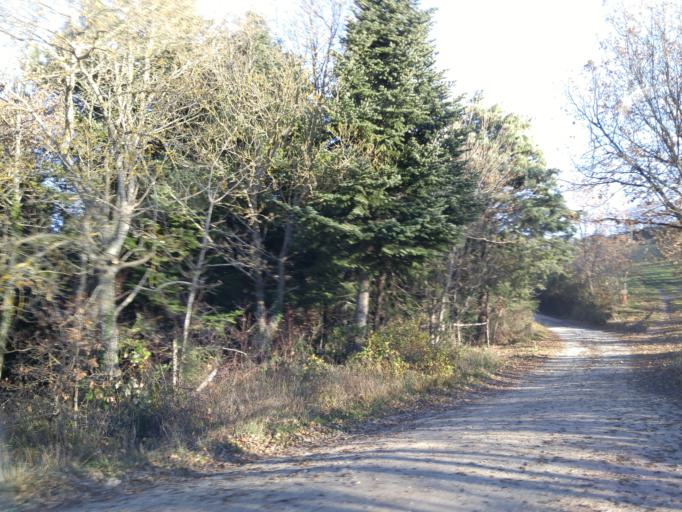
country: IT
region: The Marches
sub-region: Provincia di Pesaro e Urbino
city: Isola del Piano
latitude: 43.7721
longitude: 12.8025
